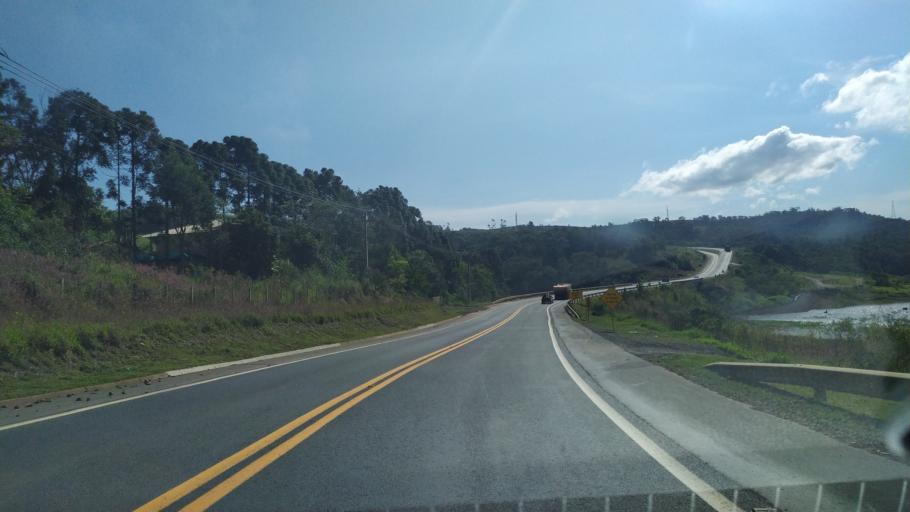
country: BR
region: Parana
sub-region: Telemaco Borba
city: Telemaco Borba
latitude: -24.2671
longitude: -50.7226
